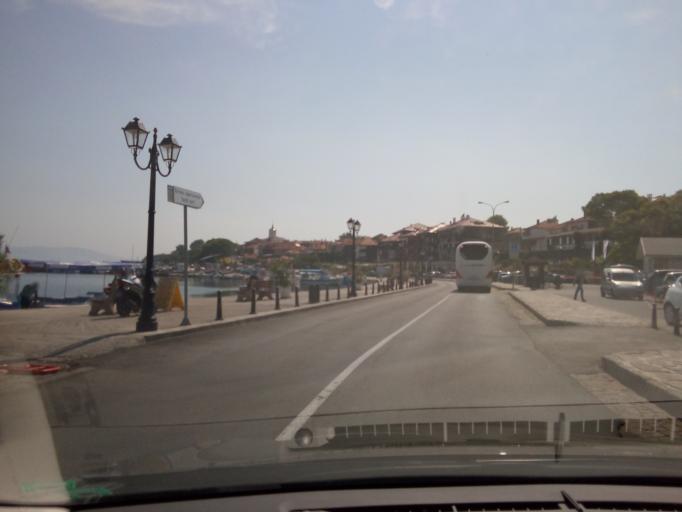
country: BG
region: Burgas
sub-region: Obshtina Nesebur
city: Nesebar
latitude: 42.6594
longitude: 27.7312
